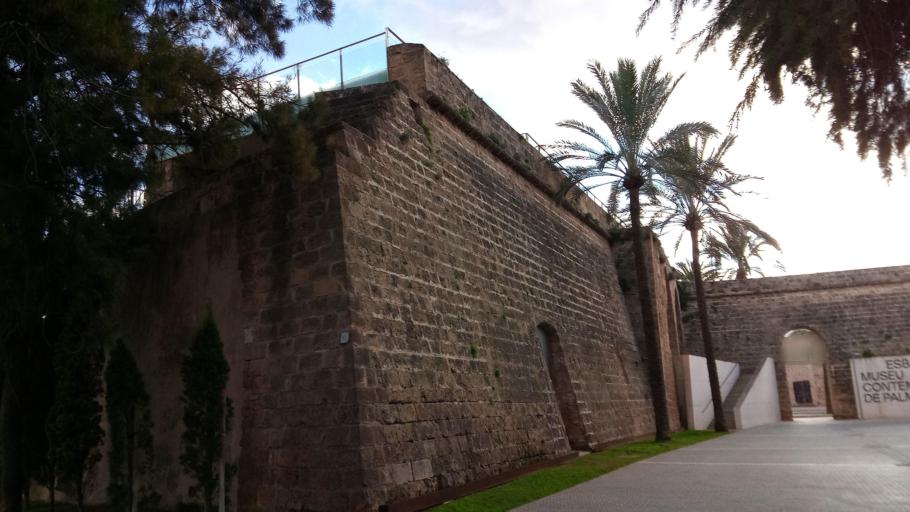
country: ES
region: Balearic Islands
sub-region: Illes Balears
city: Palma
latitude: 39.5707
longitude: 2.6421
